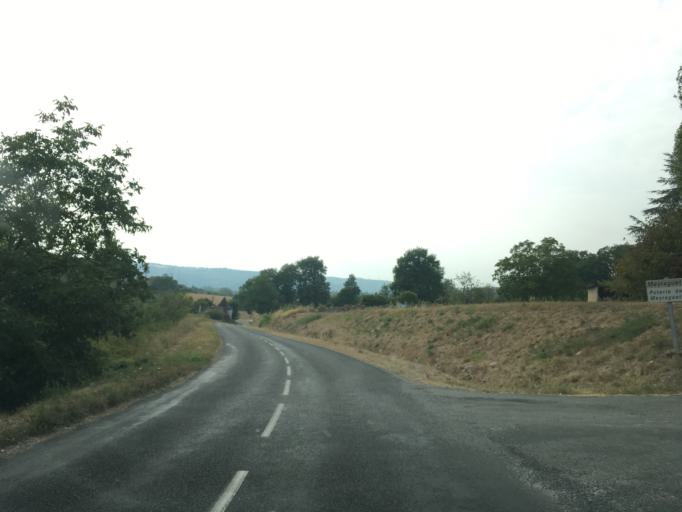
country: FR
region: Midi-Pyrenees
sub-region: Departement du Lot
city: Souillac
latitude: 44.8496
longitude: 1.5397
